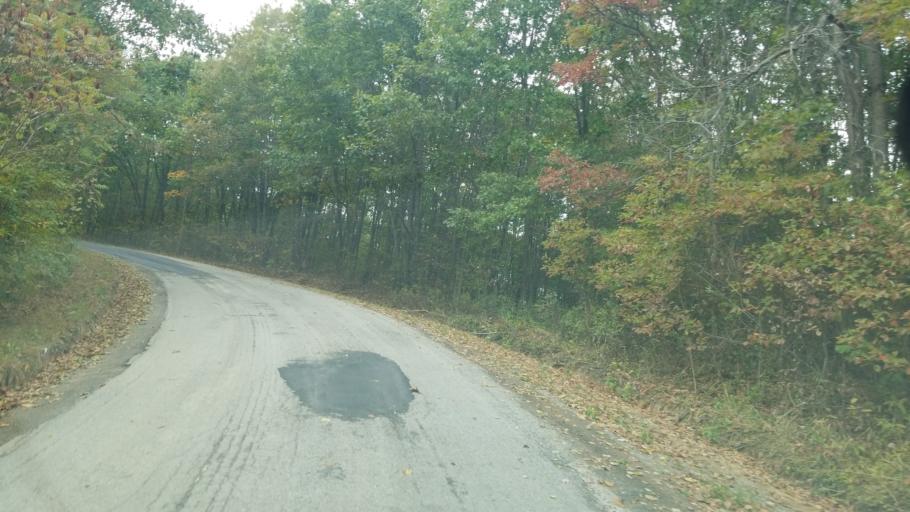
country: US
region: Ohio
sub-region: Jackson County
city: Wellston
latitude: 39.1588
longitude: -82.5936
